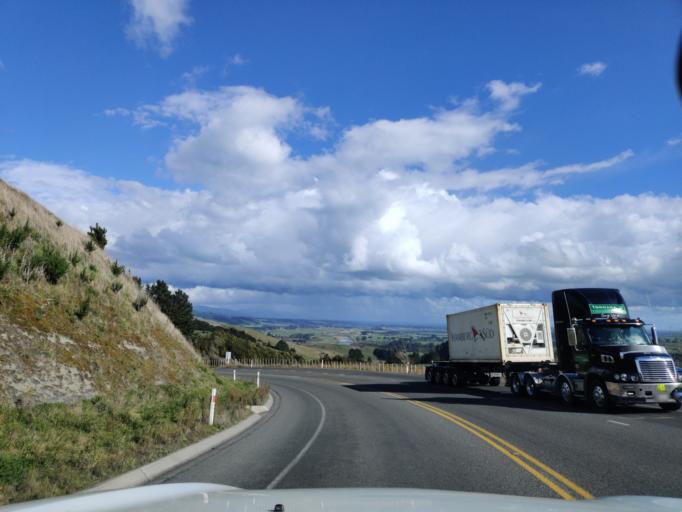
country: NZ
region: Manawatu-Wanganui
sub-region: Palmerston North City
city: Palmerston North
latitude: -40.2868
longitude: 175.7870
